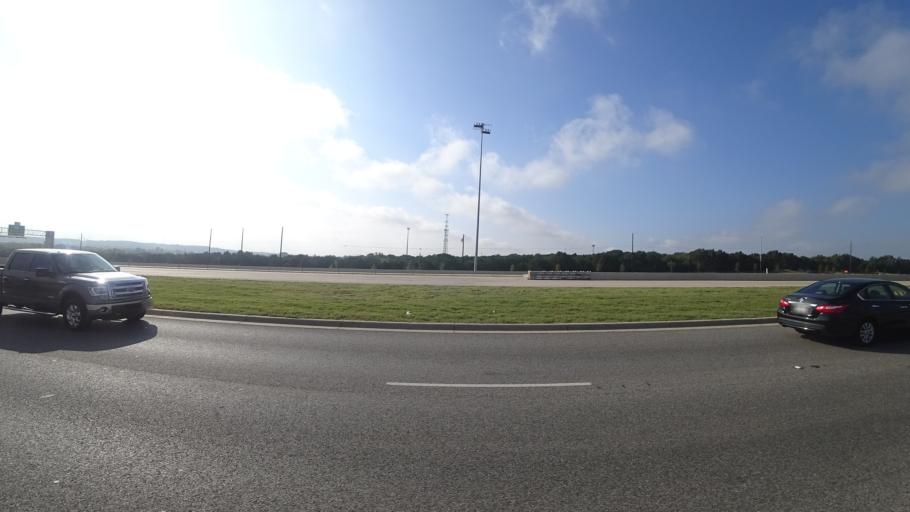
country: US
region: Texas
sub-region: Travis County
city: Austin
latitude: 30.3283
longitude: -97.6646
